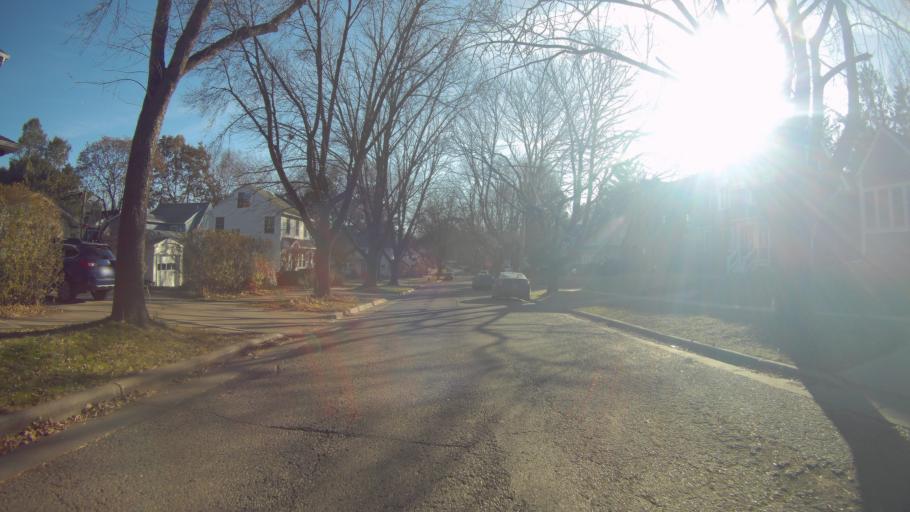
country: US
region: Wisconsin
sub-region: Dane County
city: Shorewood Hills
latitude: 43.0652
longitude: -89.4282
